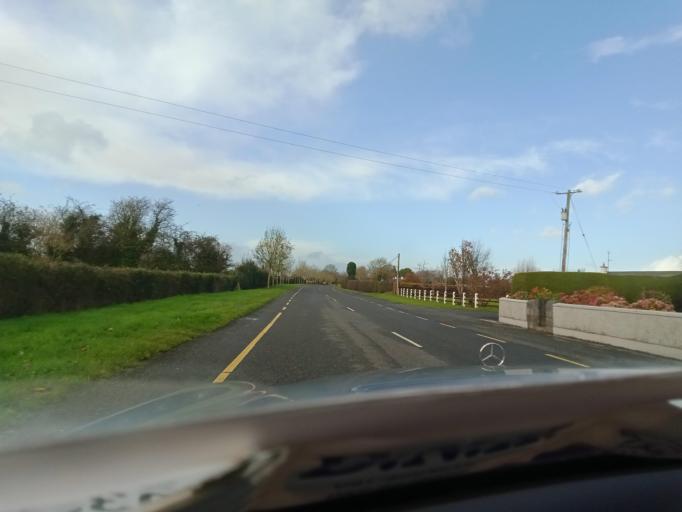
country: IE
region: Munster
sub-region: Waterford
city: Portlaw
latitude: 52.3224
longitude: -7.3051
